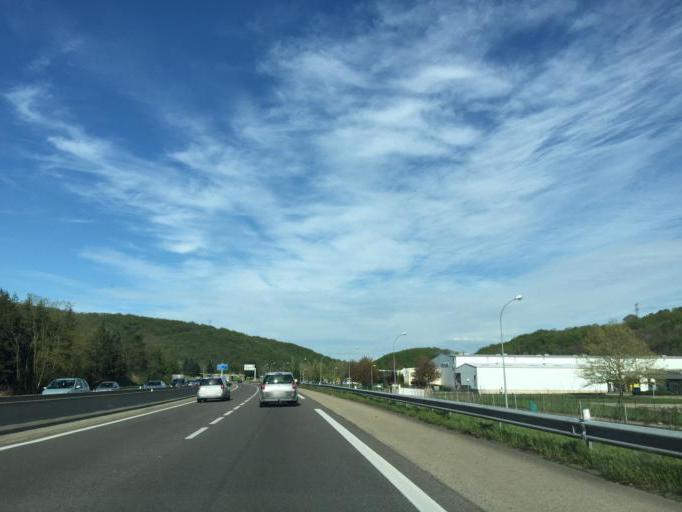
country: FR
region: Rhone-Alpes
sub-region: Departement du Rhone
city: Echalas
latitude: 45.5752
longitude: 4.7196
